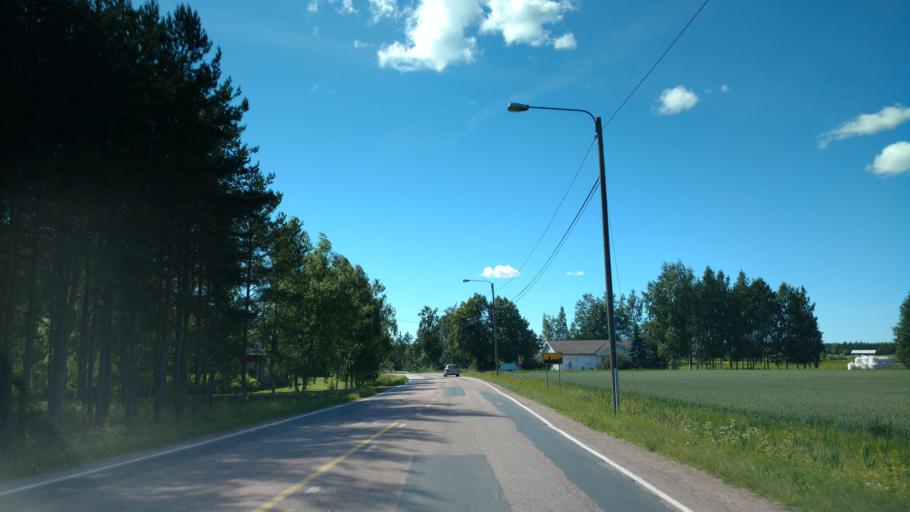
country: FI
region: Varsinais-Suomi
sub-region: Turku
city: Rusko
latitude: 60.5322
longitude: 22.2181
